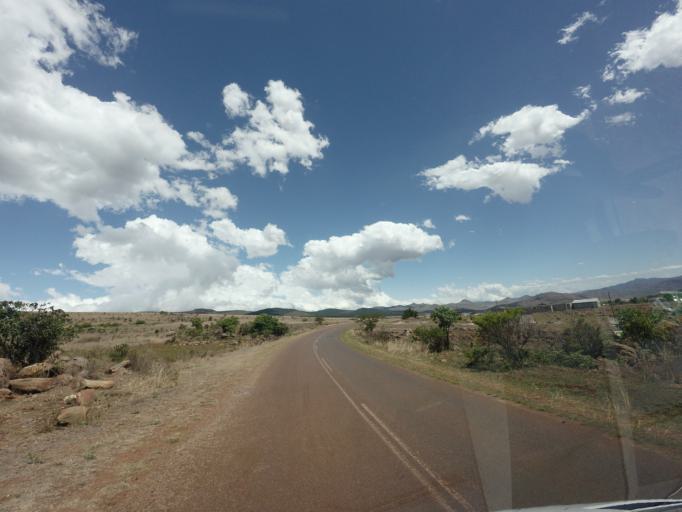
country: ZA
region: Mpumalanga
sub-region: Ehlanzeni District
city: Graksop
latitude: -24.6540
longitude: 30.8184
